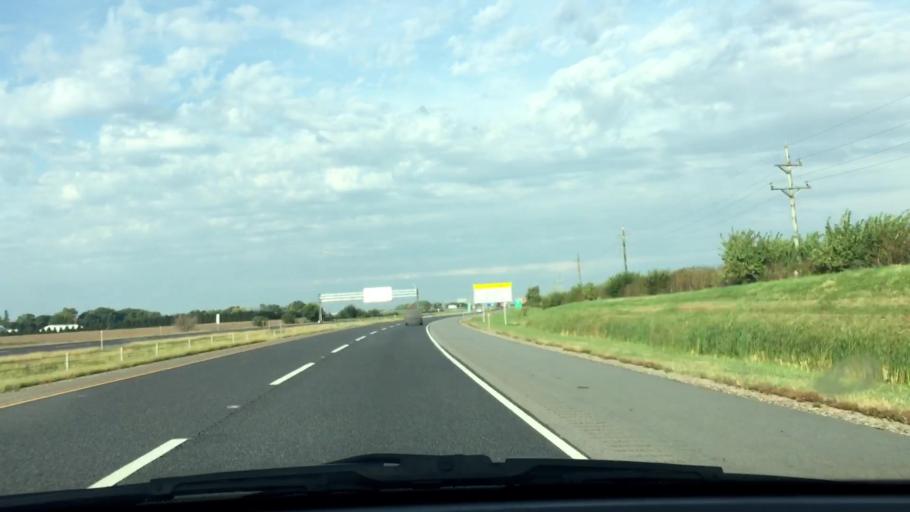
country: US
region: Illinois
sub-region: Lee County
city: Dixon
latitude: 41.8232
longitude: -89.4378
